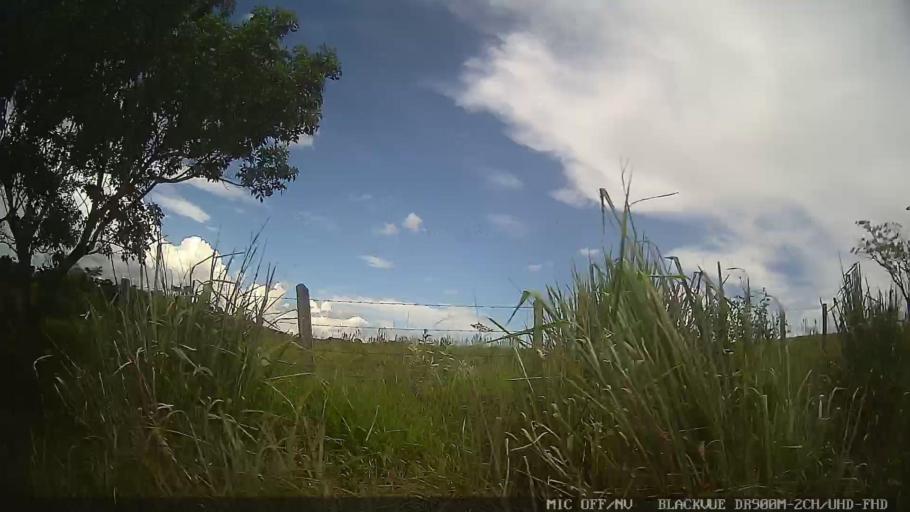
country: BR
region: Sao Paulo
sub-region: Conchas
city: Conchas
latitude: -22.9903
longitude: -47.9966
